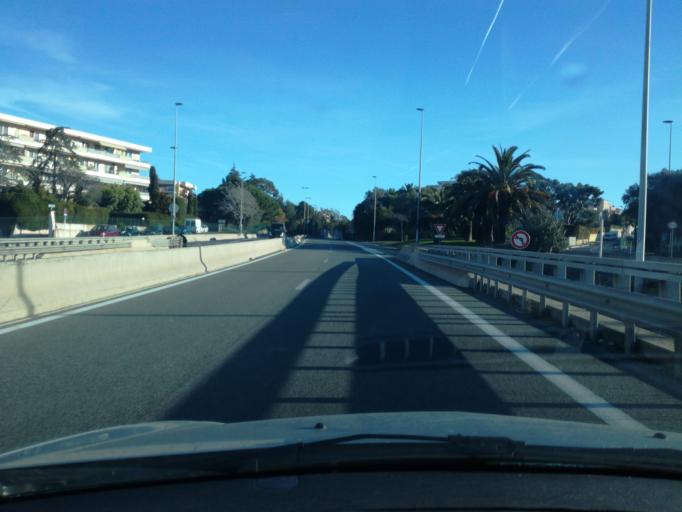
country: FR
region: Provence-Alpes-Cote d'Azur
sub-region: Departement des Alpes-Maritimes
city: Antibes
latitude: 43.5782
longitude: 7.1068
